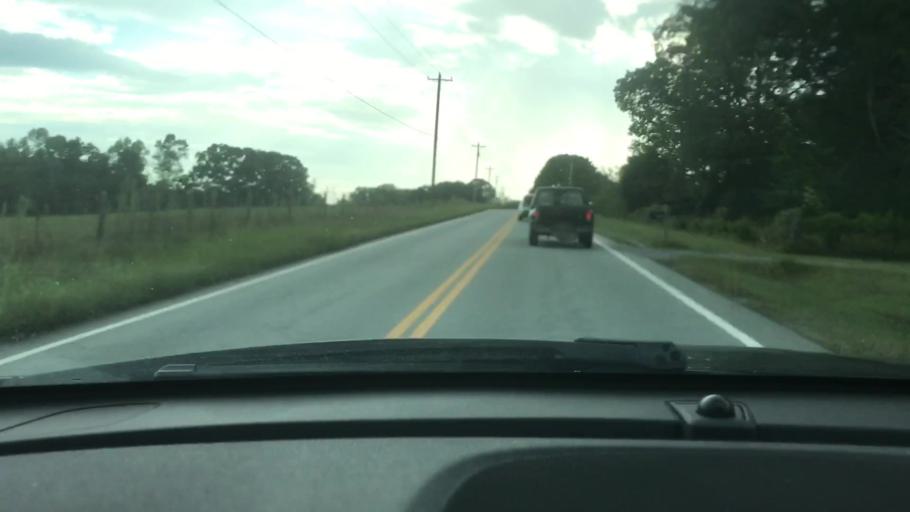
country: US
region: Tennessee
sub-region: Dickson County
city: Charlotte
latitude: 36.2131
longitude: -87.2743
